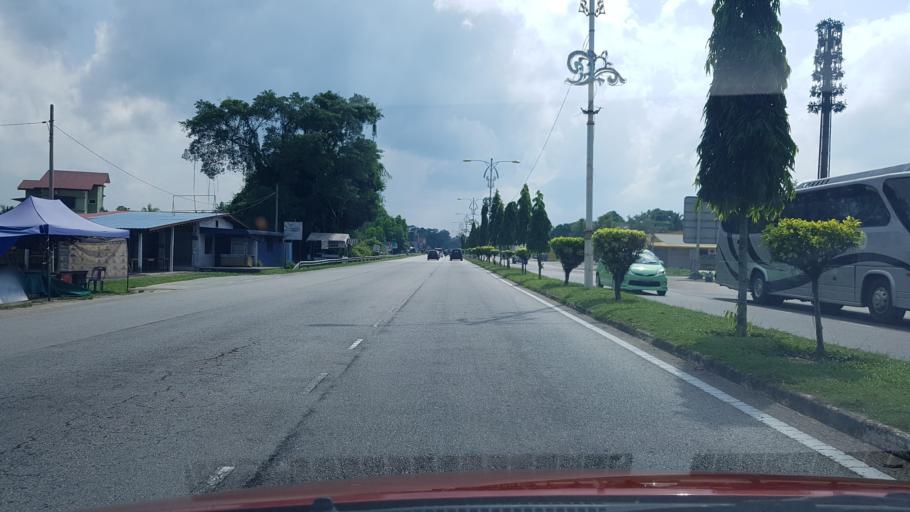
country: MY
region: Terengganu
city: Kuala Terengganu
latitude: 5.3394
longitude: 103.1044
